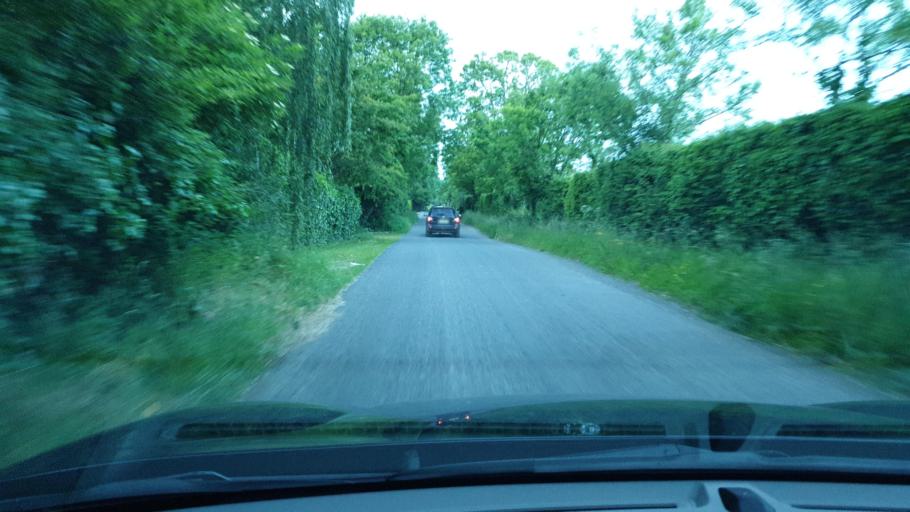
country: IE
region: Leinster
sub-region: An Mhi
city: Ashbourne
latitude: 53.5754
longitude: -6.3502
